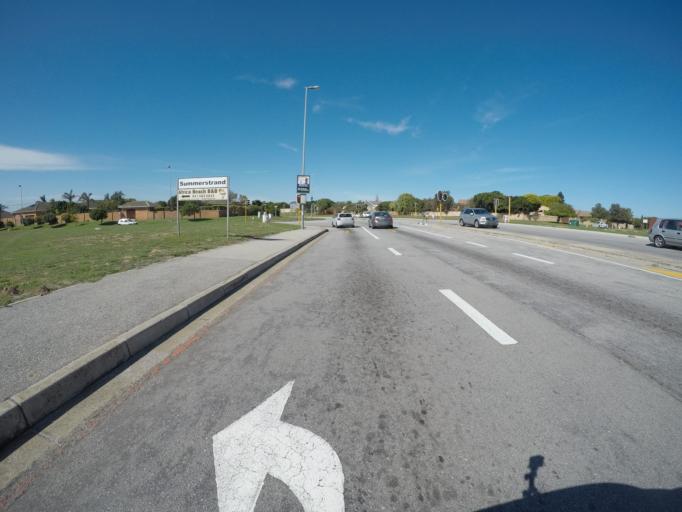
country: ZA
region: Eastern Cape
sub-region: Nelson Mandela Bay Metropolitan Municipality
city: Port Elizabeth
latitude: -33.9912
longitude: 25.6480
